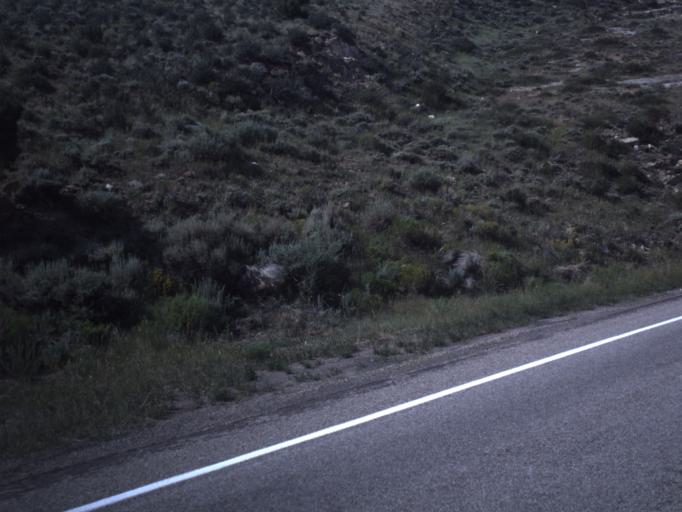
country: US
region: Utah
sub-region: Daggett County
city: Manila
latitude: 40.9086
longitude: -109.6995
